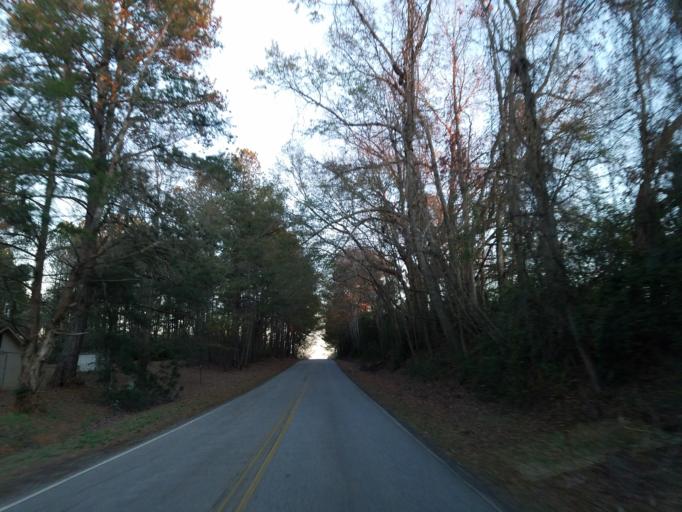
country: US
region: Georgia
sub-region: Monroe County
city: Forsyth
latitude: 33.0115
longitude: -83.9055
